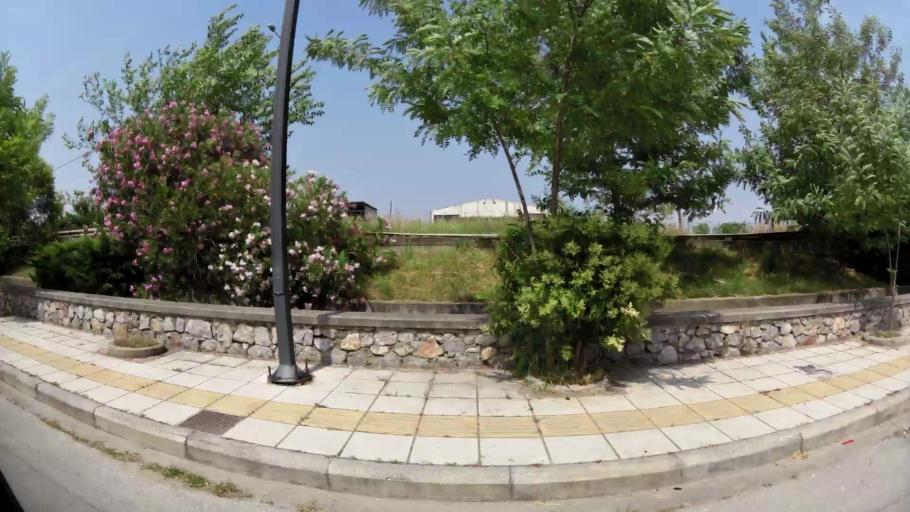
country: GR
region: Central Macedonia
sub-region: Nomos Thessalonikis
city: Diavata
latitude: 40.6894
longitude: 22.8608
